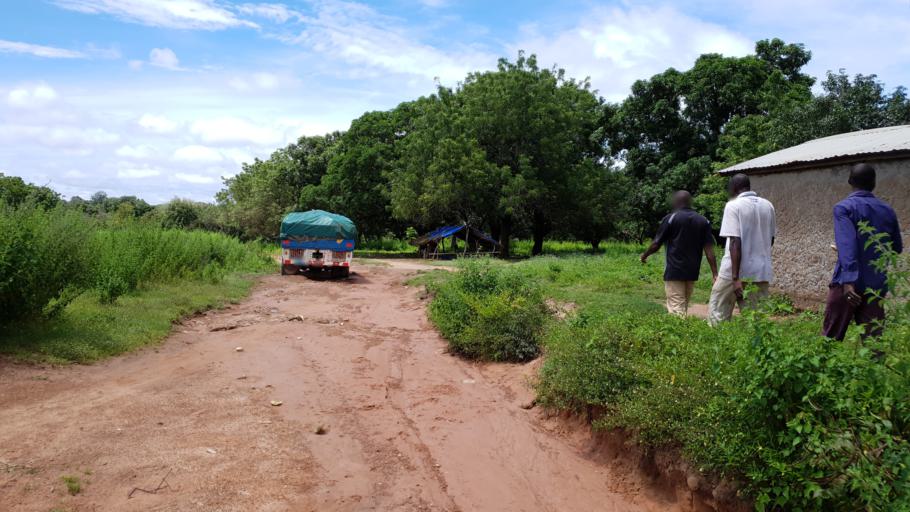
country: CI
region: Savanes
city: Tengrela
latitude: 10.3574
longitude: -6.9184
